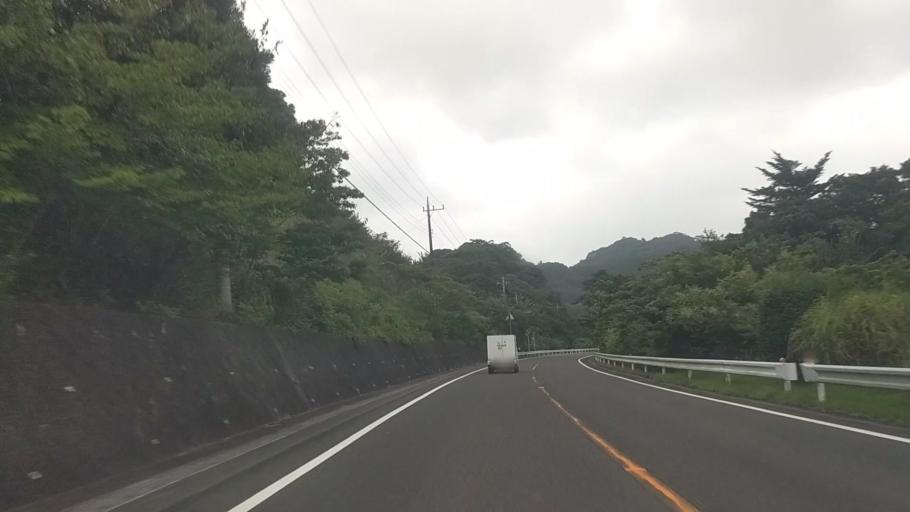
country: JP
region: Chiba
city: Kawaguchi
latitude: 35.1604
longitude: 140.0648
